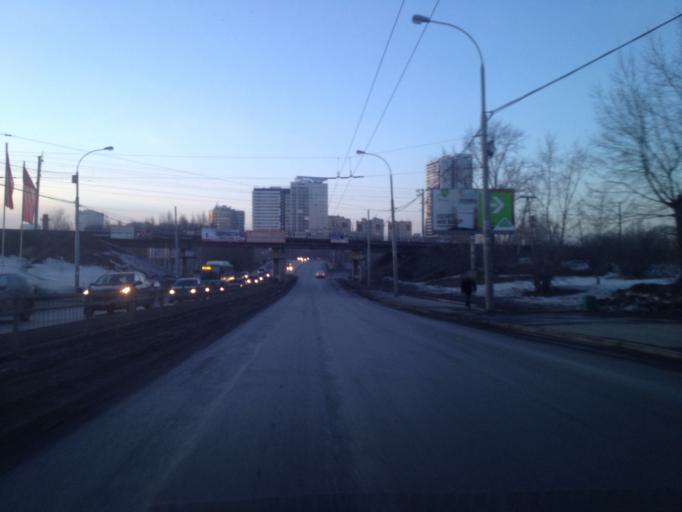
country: RU
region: Sverdlovsk
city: Yekaterinburg
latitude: 56.7929
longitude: 60.6426
